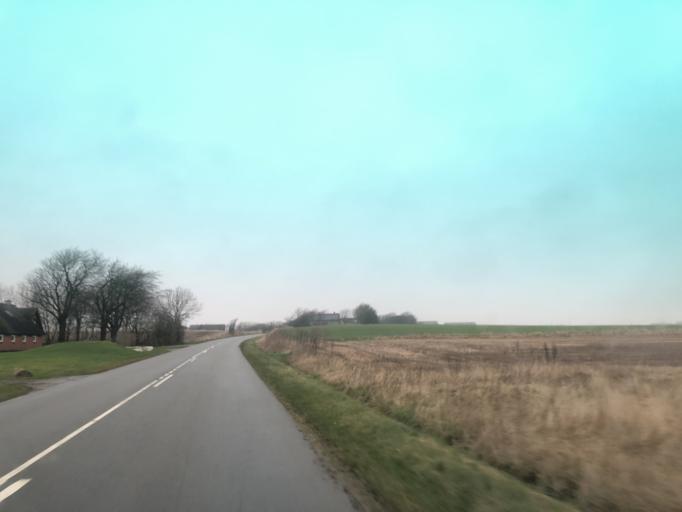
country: DK
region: North Denmark
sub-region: Thisted Kommune
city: Hurup
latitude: 56.7330
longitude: 8.4155
